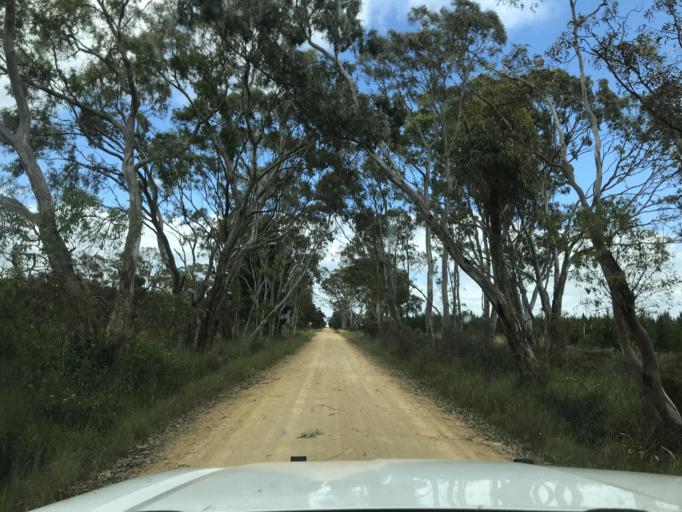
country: AU
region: South Australia
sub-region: Wattle Range
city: Penola
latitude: -37.3169
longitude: 141.1240
